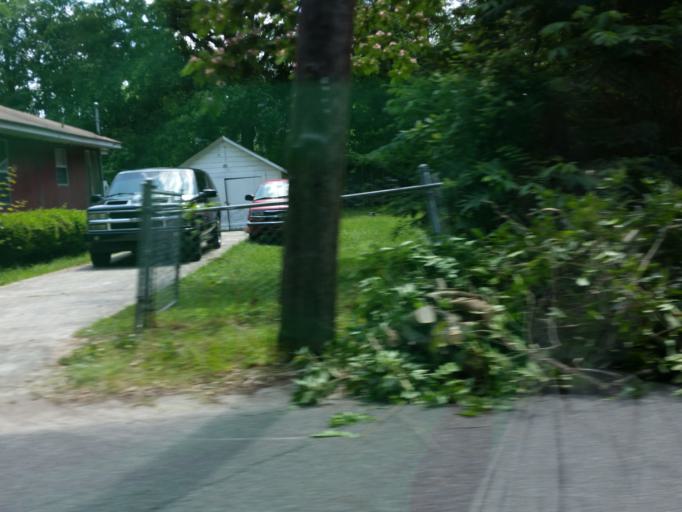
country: US
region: Mississippi
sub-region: Lauderdale County
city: Meridian
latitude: 32.3821
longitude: -88.7204
